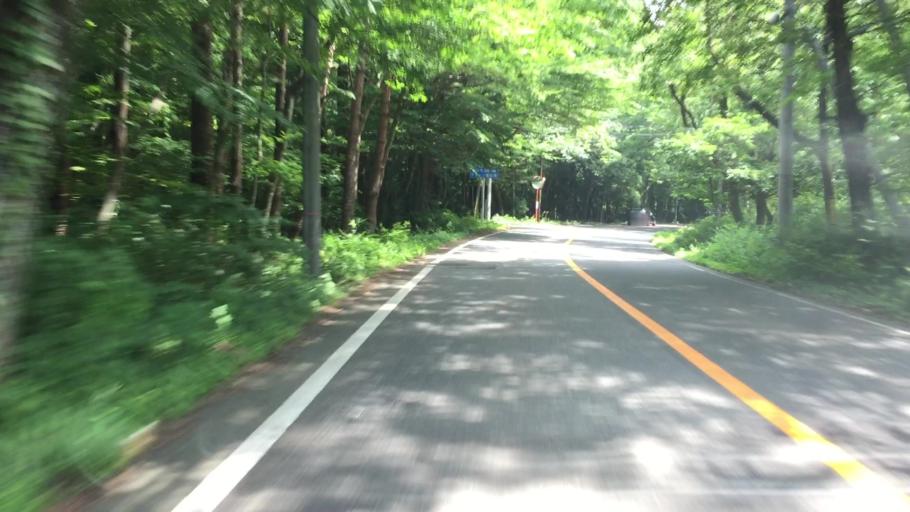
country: JP
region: Tochigi
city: Kuroiso
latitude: 37.0422
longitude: 139.9419
